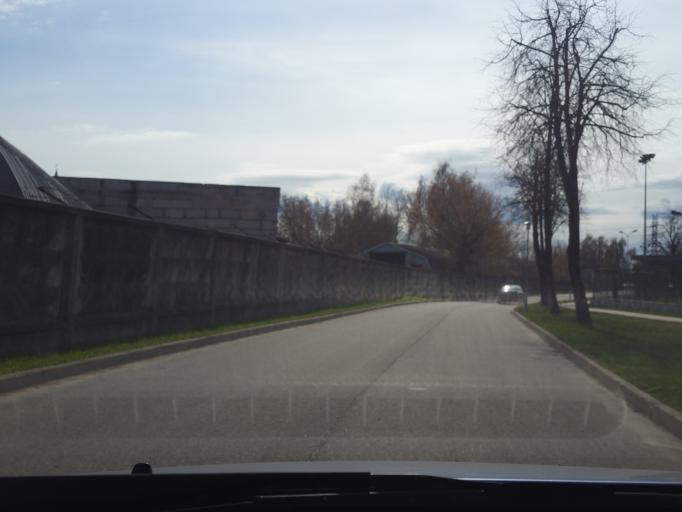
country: LV
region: Riga
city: Jaunciems
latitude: 56.9871
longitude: 24.1956
